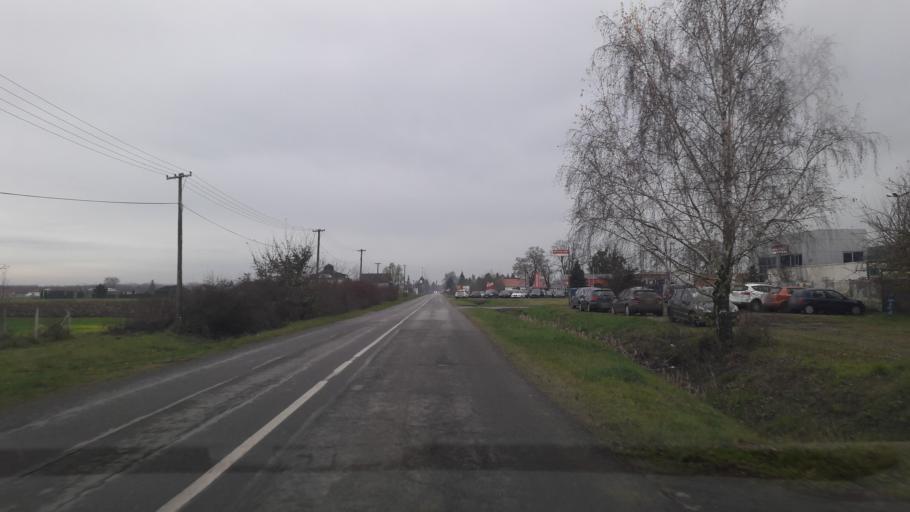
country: HR
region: Osjecko-Baranjska
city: Josipovac
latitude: 45.5924
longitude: 18.5696
